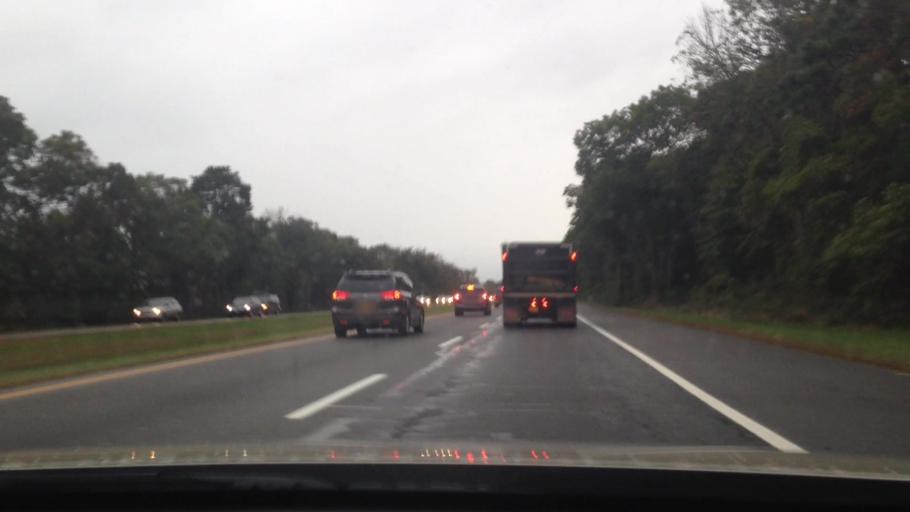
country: US
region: New York
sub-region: Suffolk County
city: Holtsville
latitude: 40.8292
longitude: -73.0555
